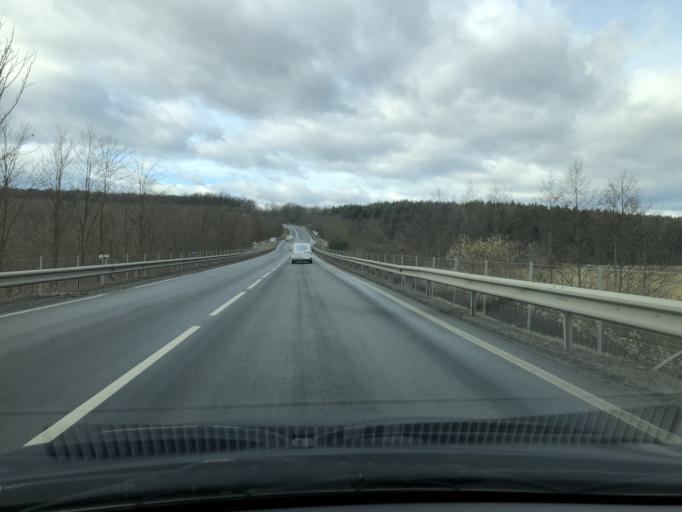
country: AT
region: Burgenland
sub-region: Politischer Bezirk Oberwart
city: Hannersdorf
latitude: 47.2608
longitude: 16.3699
